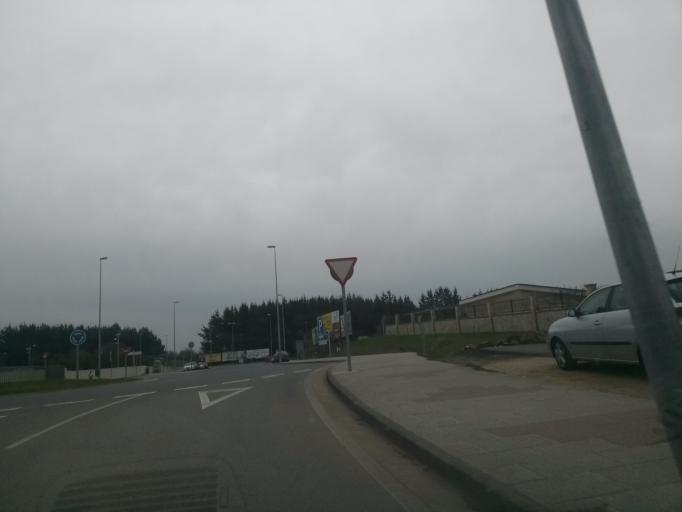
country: ES
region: Galicia
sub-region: Provincia de Lugo
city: Lugo
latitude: 43.0191
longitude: -7.5383
